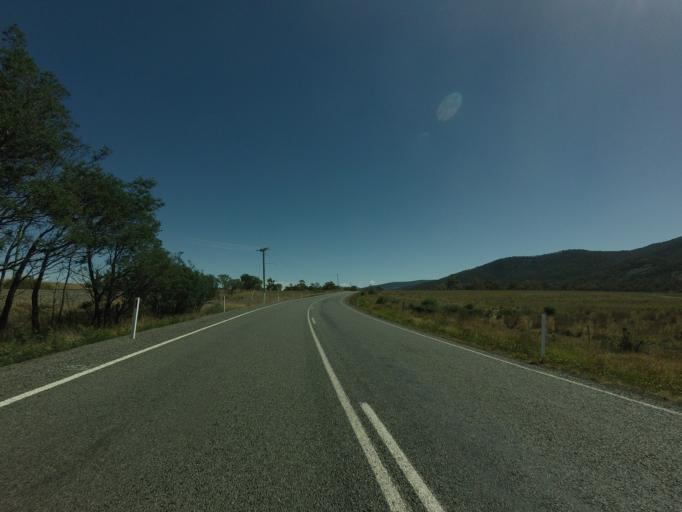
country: AU
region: Tasmania
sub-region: Northern Midlands
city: Evandale
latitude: -41.7519
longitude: 147.7737
